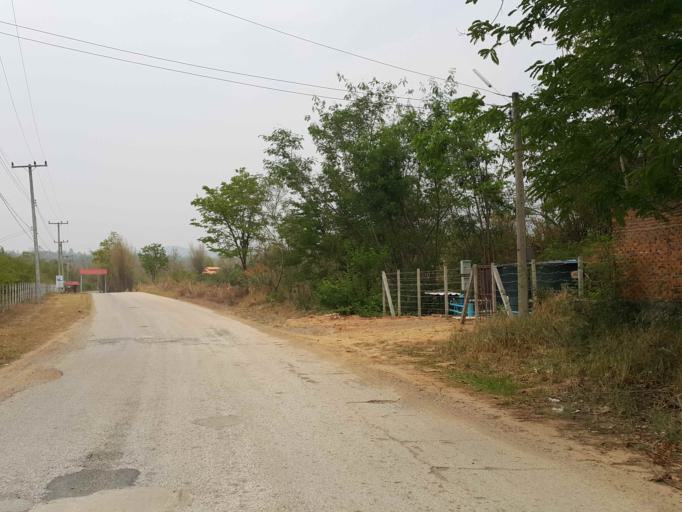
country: TH
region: Chiang Mai
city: San Sai
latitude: 18.9341
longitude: 99.0129
